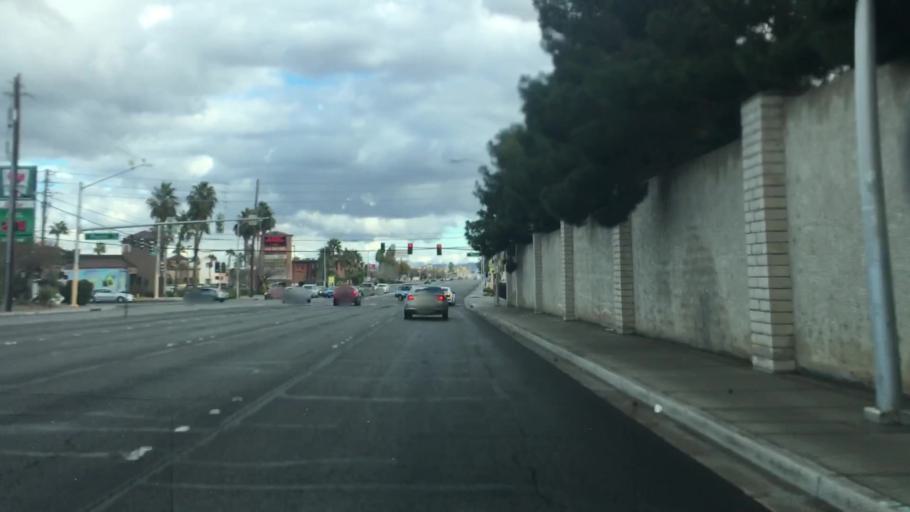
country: US
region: Nevada
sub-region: Clark County
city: Whitney
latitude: 36.0715
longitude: -115.1018
